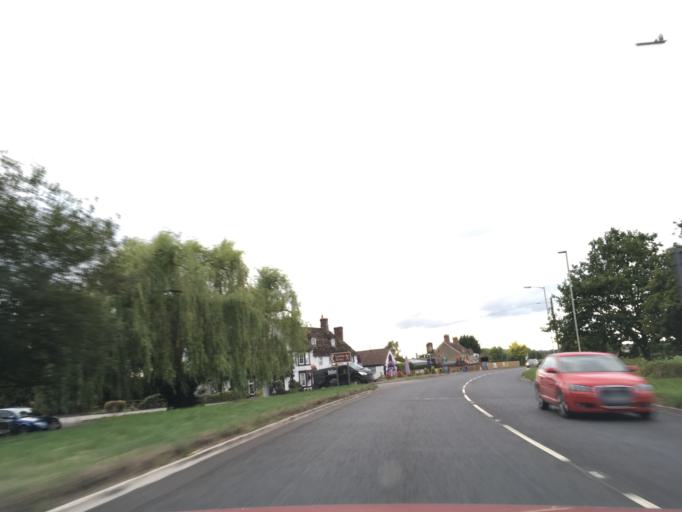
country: GB
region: England
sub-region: Wiltshire
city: Bremhill
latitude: 51.4388
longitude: -2.0742
